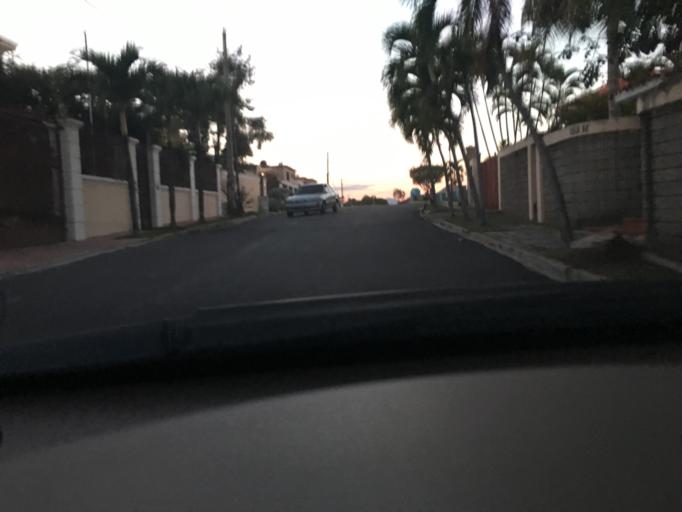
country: DO
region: Nacional
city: Santo Domingo
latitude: 18.4894
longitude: -69.9651
